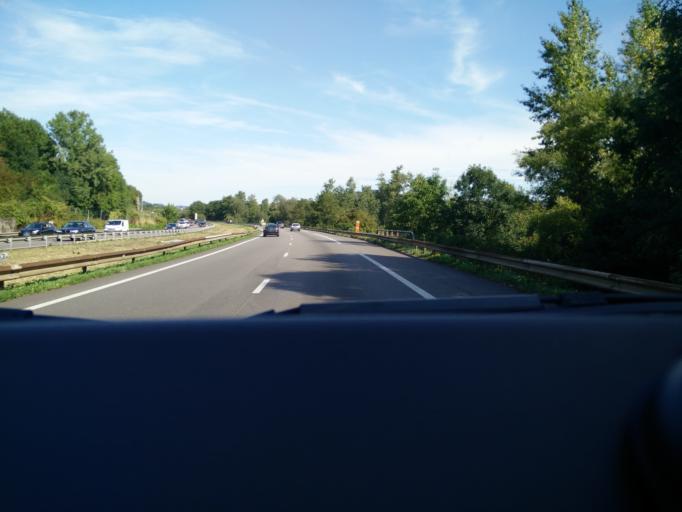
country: FR
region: Lorraine
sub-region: Departement de Meurthe-et-Moselle
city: Pompey
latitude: 48.7912
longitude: 6.1235
